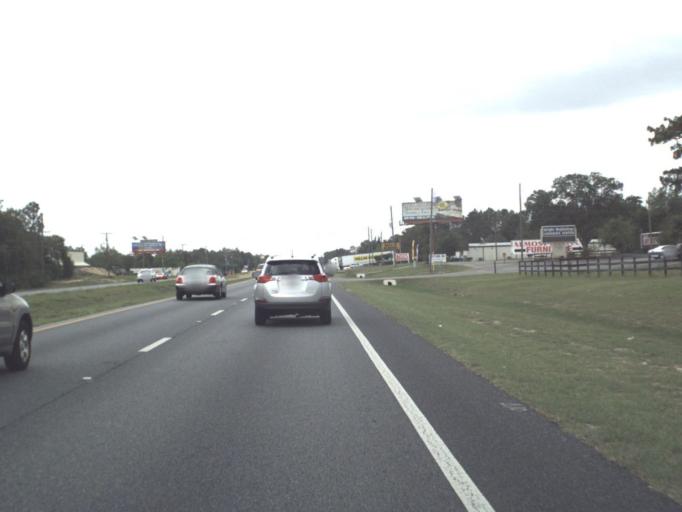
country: US
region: Florida
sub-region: Marion County
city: Belleview
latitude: 29.0052
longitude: -82.0045
